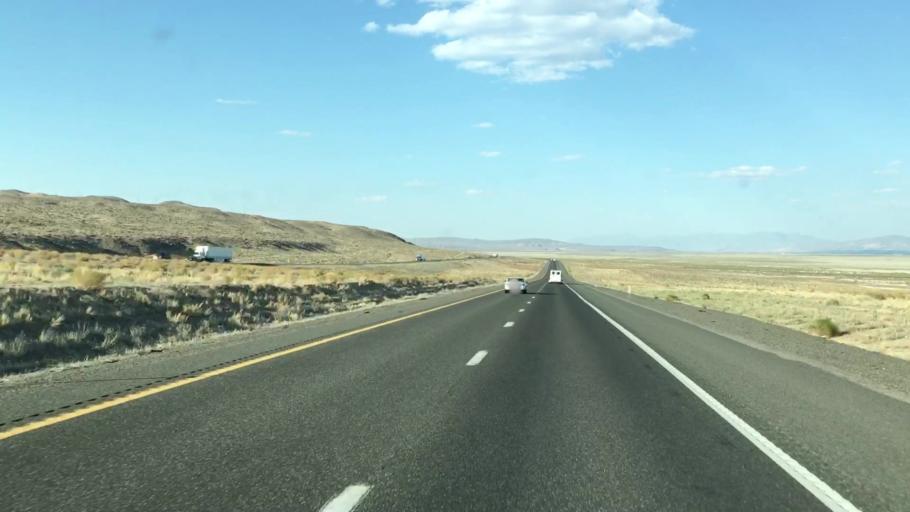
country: US
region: Nevada
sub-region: Pershing County
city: Lovelock
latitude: 39.9757
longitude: -118.6944
